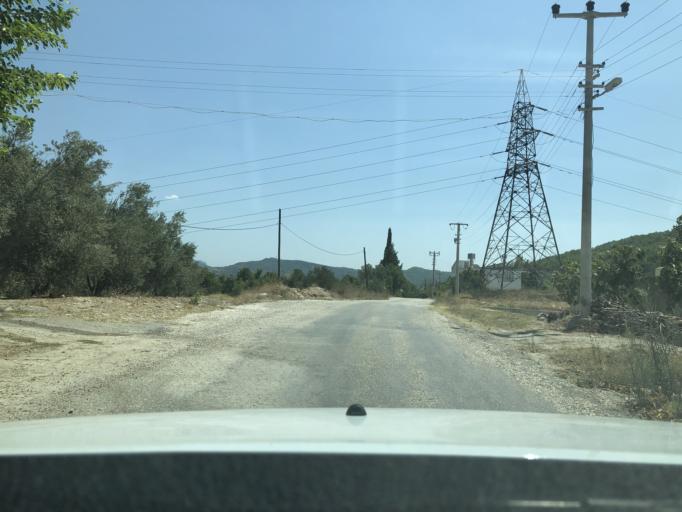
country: TR
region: Antalya
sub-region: Manavgat
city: Kizilagac
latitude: 36.8575
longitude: 31.5567
